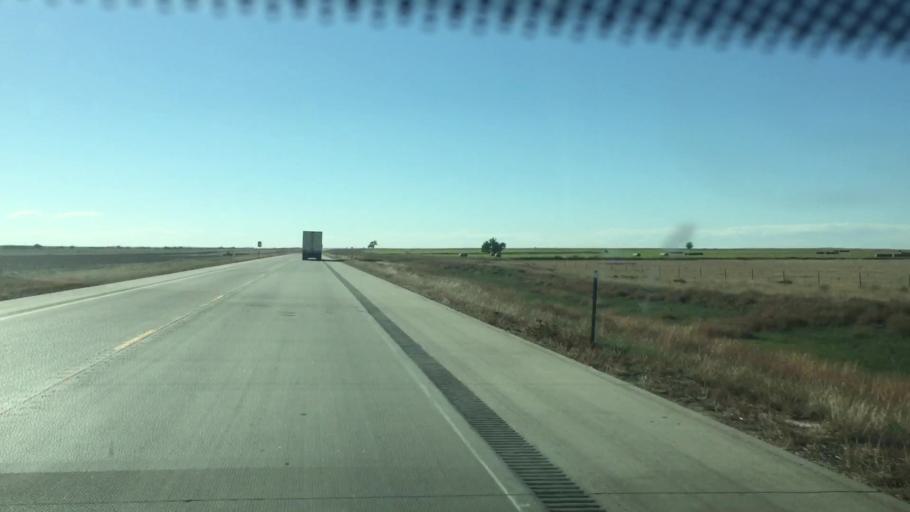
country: US
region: Colorado
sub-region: Kiowa County
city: Eads
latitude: 38.7640
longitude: -102.8114
